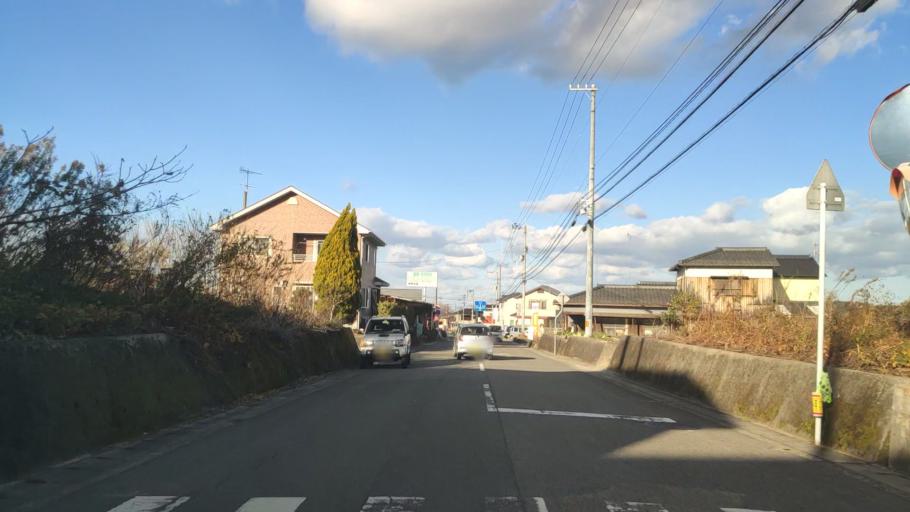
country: JP
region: Ehime
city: Saijo
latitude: 33.8922
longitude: 133.1318
